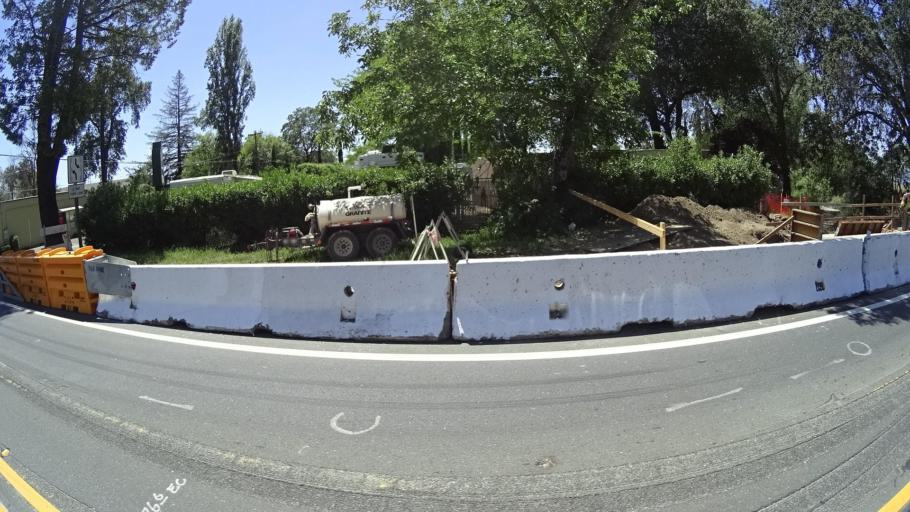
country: US
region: California
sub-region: Lake County
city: Lucerne
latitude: 39.0957
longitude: -122.8012
